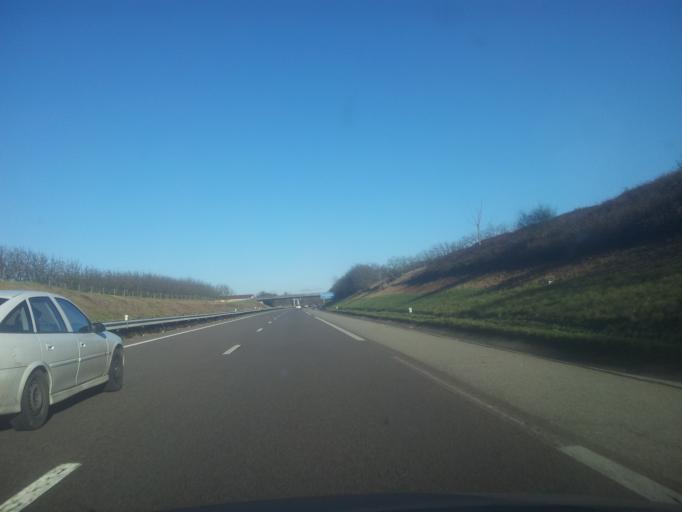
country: FR
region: Rhone-Alpes
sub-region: Departement de l'Isere
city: Saint-Sauveur
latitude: 45.1428
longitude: 5.3403
